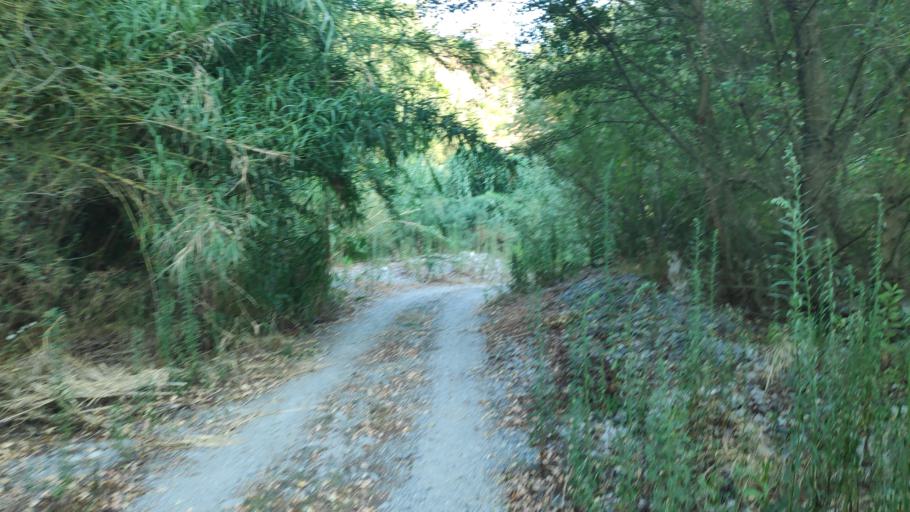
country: IT
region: Calabria
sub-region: Provincia di Reggio Calabria
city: Placanica
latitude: 38.4156
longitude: 16.4371
